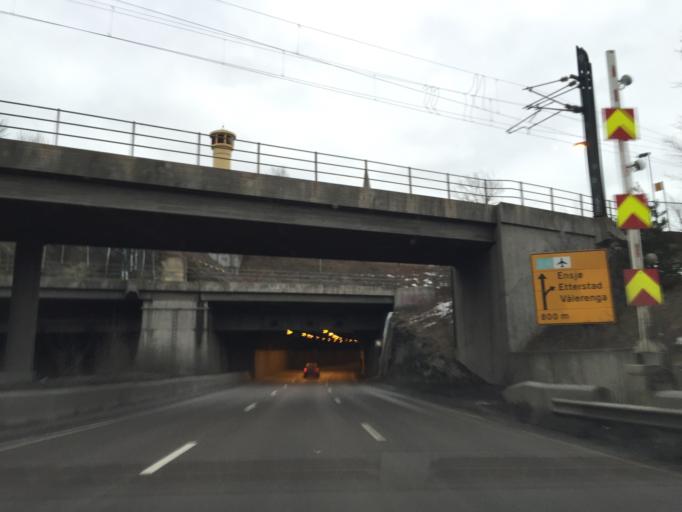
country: NO
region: Oslo
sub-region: Oslo
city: Oslo
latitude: 59.9050
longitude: 10.7852
